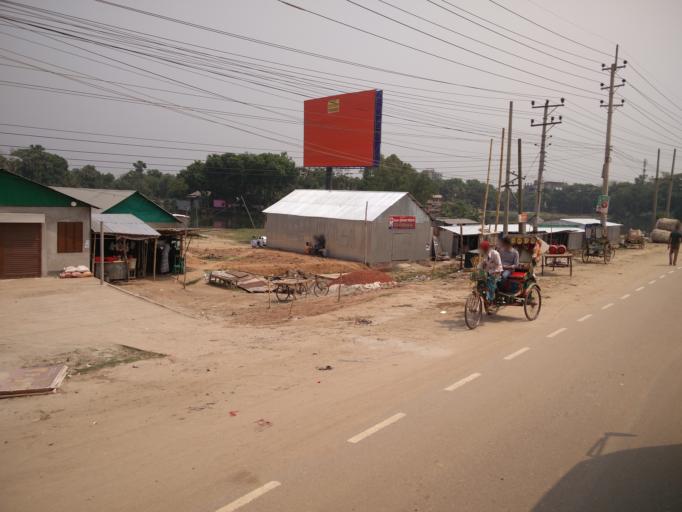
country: BD
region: Dhaka
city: Gafargaon
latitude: 24.4032
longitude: 90.3866
